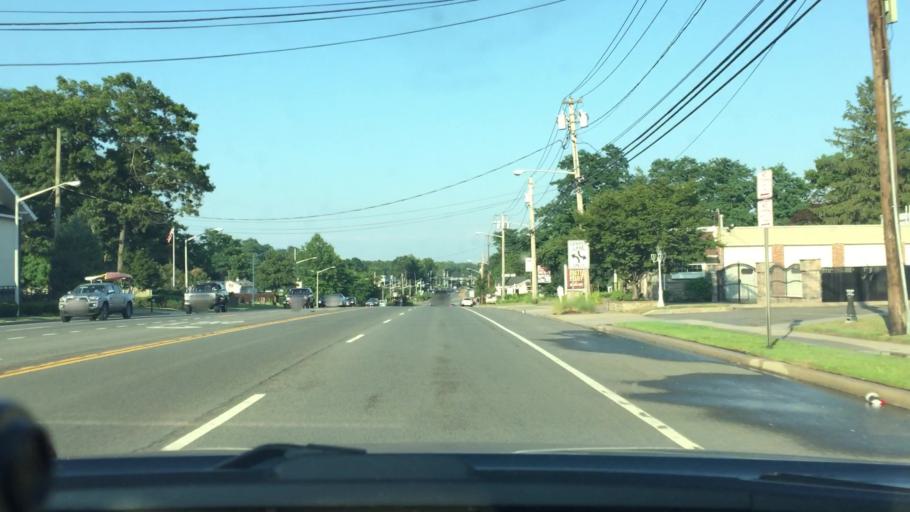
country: US
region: New York
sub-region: Suffolk County
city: Sound Beach
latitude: 40.9443
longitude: -72.9662
